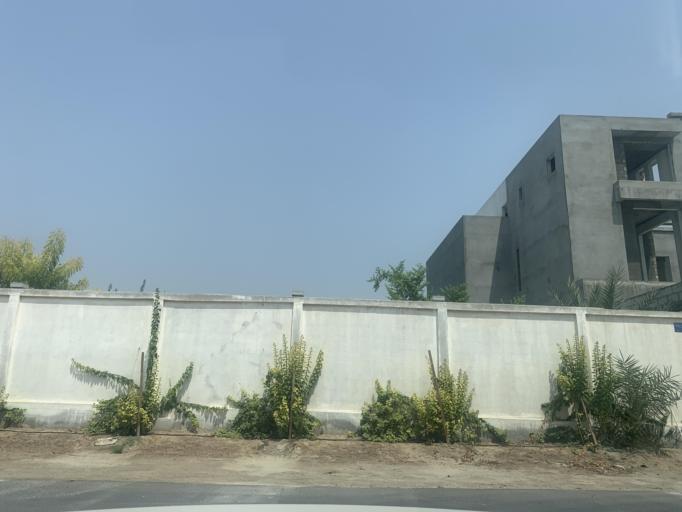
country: BH
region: Central Governorate
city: Madinat Hamad
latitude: 26.1469
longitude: 50.4759
